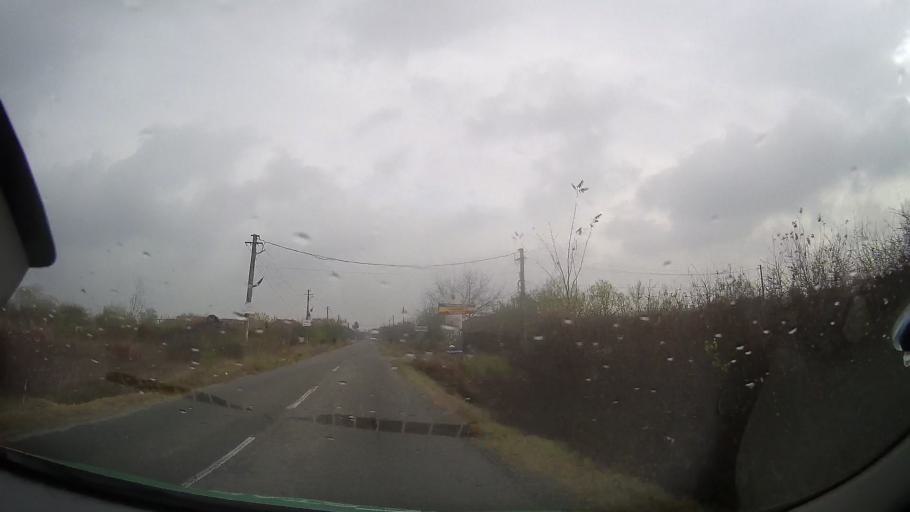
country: RO
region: Prahova
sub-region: Comuna Draganesti
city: Draganesti
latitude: 44.8297
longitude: 26.2773
